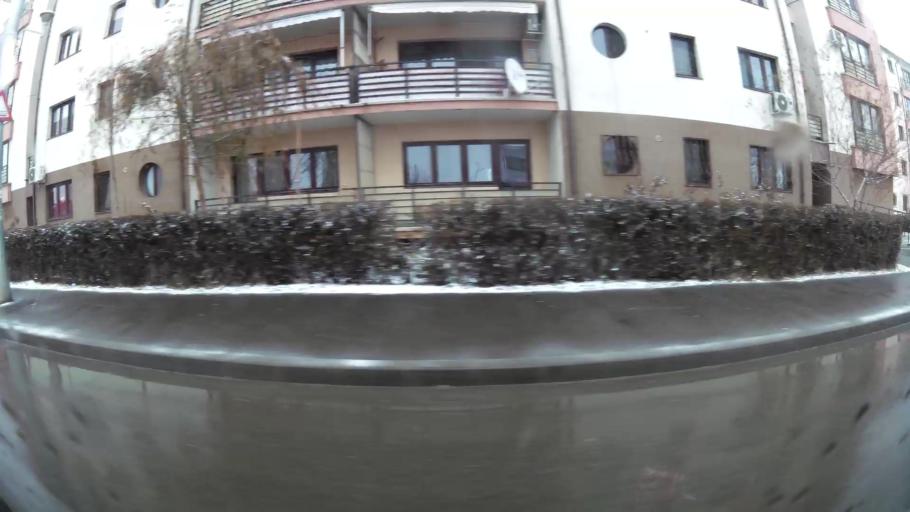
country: RO
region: Prahova
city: Ploiesti
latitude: 44.9267
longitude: 25.9948
